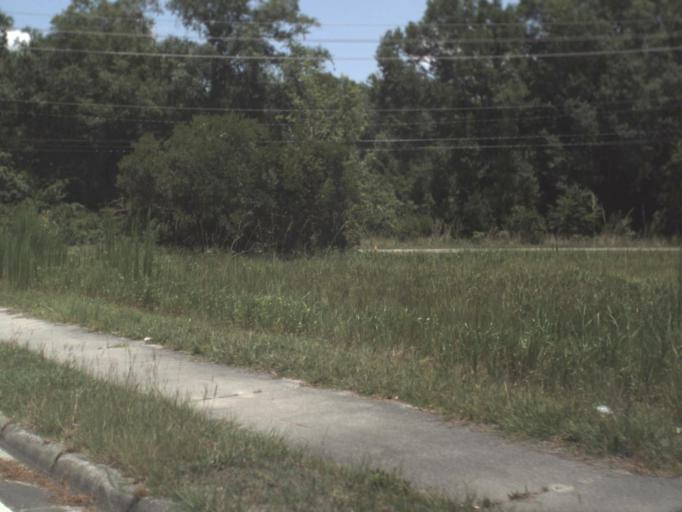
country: US
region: Florida
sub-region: Bradford County
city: Starke
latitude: 29.9528
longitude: -82.1125
